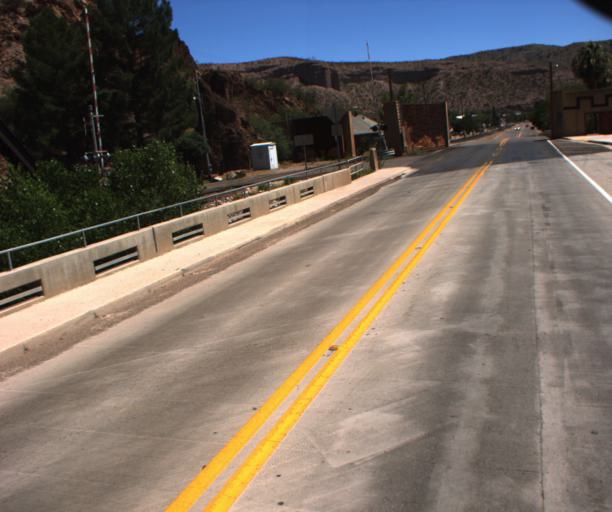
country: US
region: Arizona
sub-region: Greenlee County
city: Clifton
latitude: 33.0496
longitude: -109.2952
